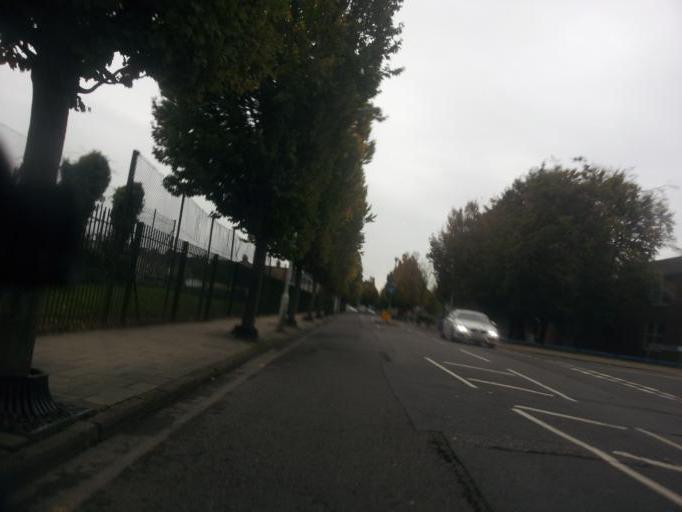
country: GB
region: England
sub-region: Kent
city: Sittingbourne
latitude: 51.3380
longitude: 0.7346
